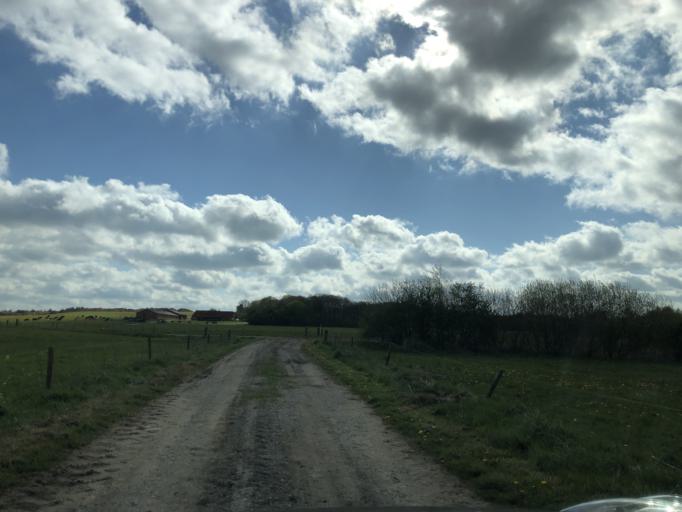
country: DK
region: Central Jutland
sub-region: Herning Kommune
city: Avlum
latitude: 56.2978
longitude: 8.7591
